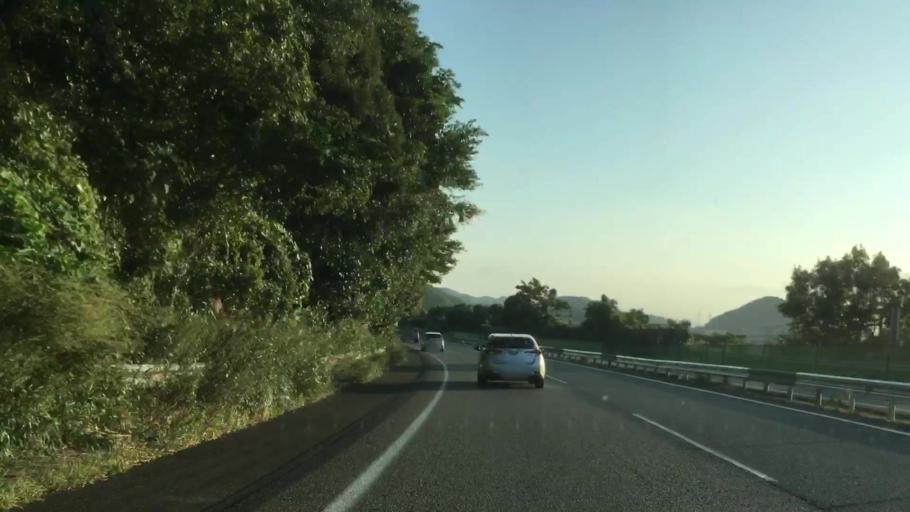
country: JP
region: Yamaguchi
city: Shimonoseki
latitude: 34.0195
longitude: 130.9582
